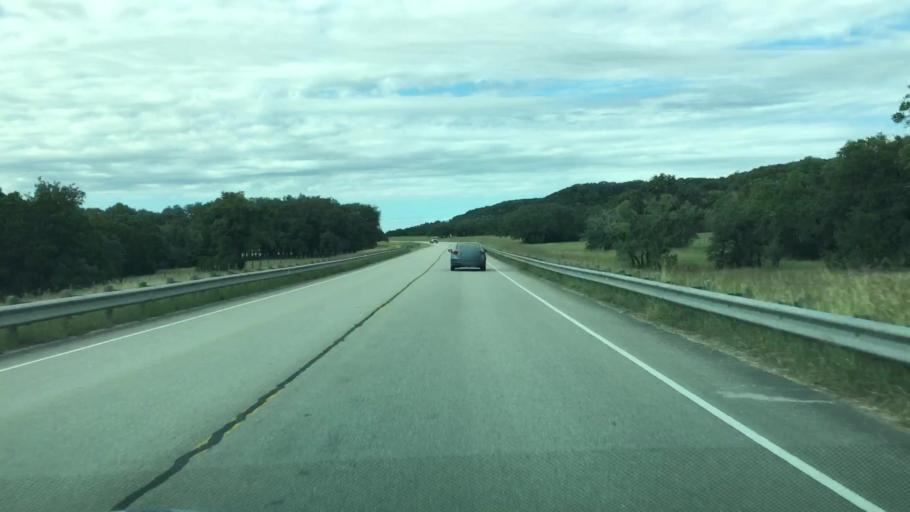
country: US
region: Texas
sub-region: Hays County
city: Wimberley
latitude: 30.0133
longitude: -98.0849
